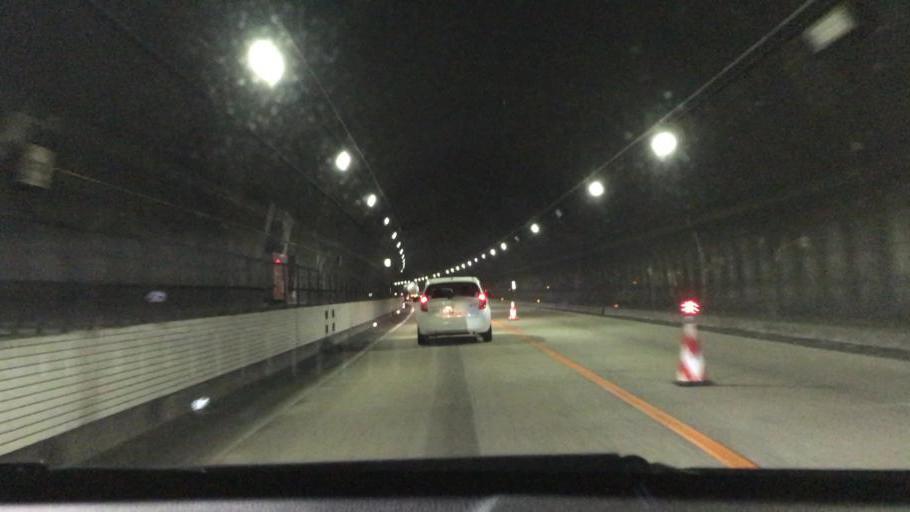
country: JP
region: Yamaguchi
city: Tokuyama
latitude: 34.0906
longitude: 131.7703
